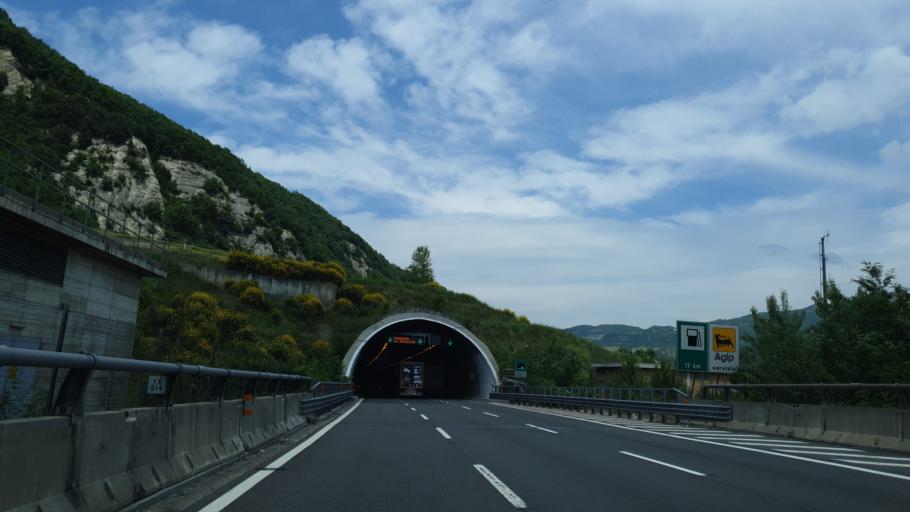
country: IT
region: Emilia-Romagna
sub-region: Provincia di Bologna
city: Vado
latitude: 44.3232
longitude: 11.2549
